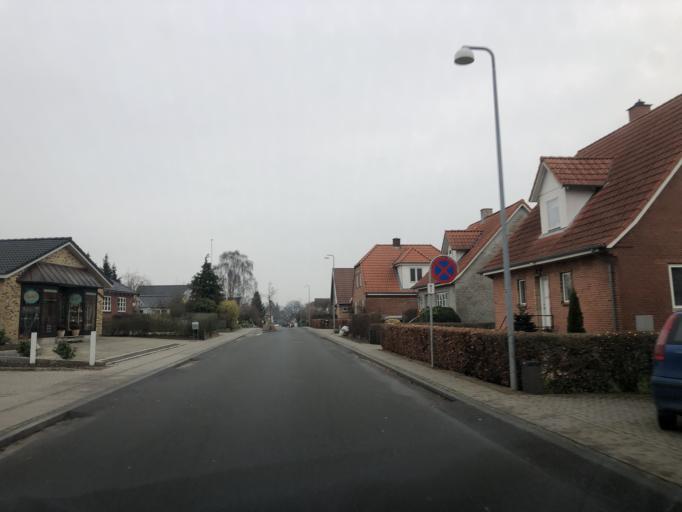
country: DK
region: South Denmark
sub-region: Faaborg-Midtfyn Kommune
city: Arslev
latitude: 55.3062
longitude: 10.4812
